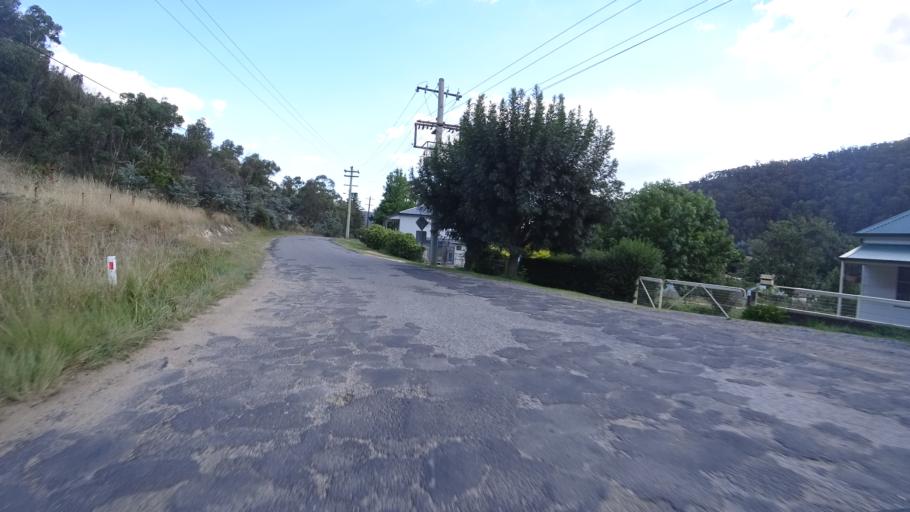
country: AU
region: New South Wales
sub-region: Lithgow
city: Lithgow
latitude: -33.4657
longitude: 150.1683
